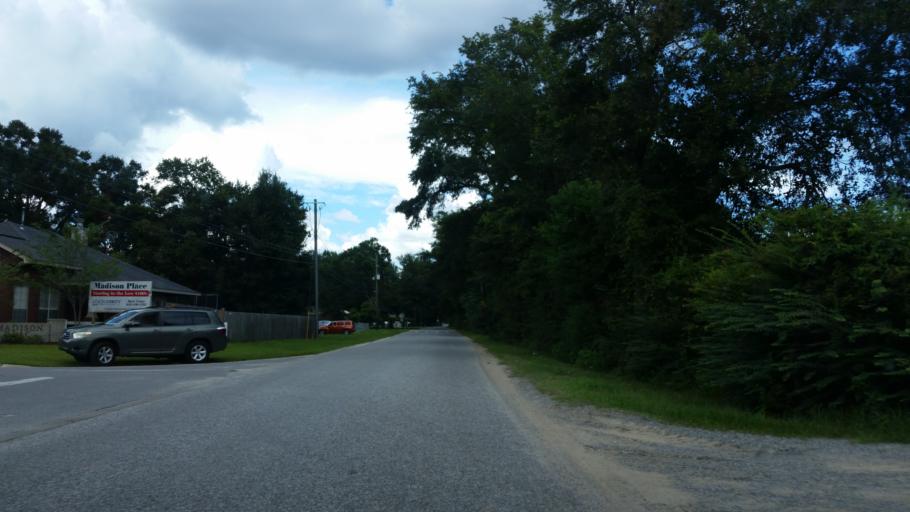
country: US
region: Florida
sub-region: Escambia County
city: Ensley
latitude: 30.5406
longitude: -87.2664
